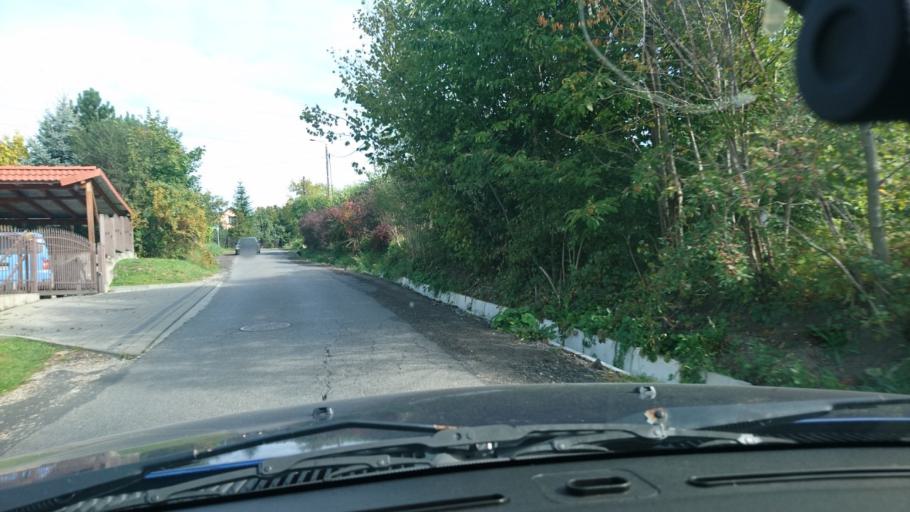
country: PL
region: Silesian Voivodeship
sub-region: Powiat bielski
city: Jaworze
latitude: 49.8132
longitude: 18.9903
